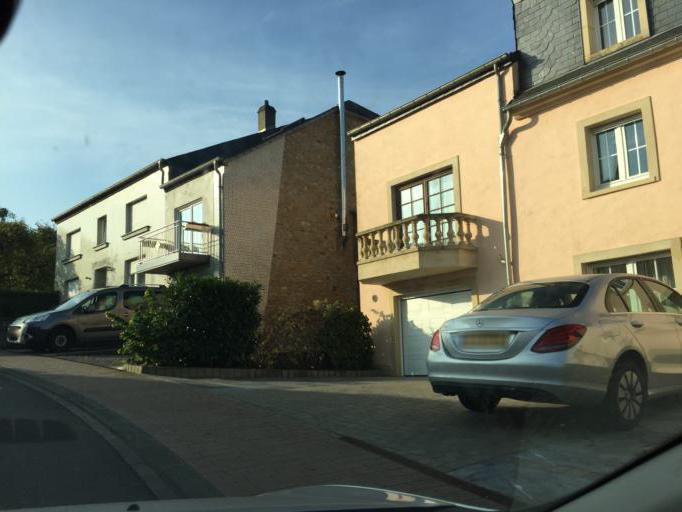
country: LU
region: Luxembourg
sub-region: Canton de Luxembourg
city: Contern
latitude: 49.5646
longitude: 6.2186
